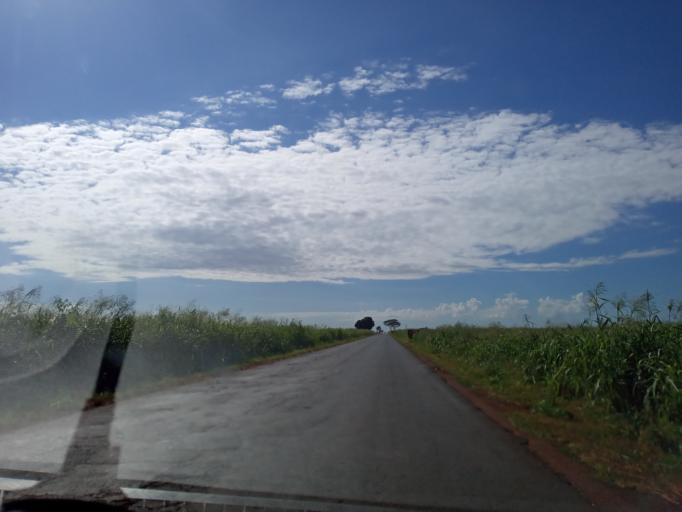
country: BR
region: Goias
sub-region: Itumbiara
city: Itumbiara
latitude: -18.4493
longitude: -49.1638
